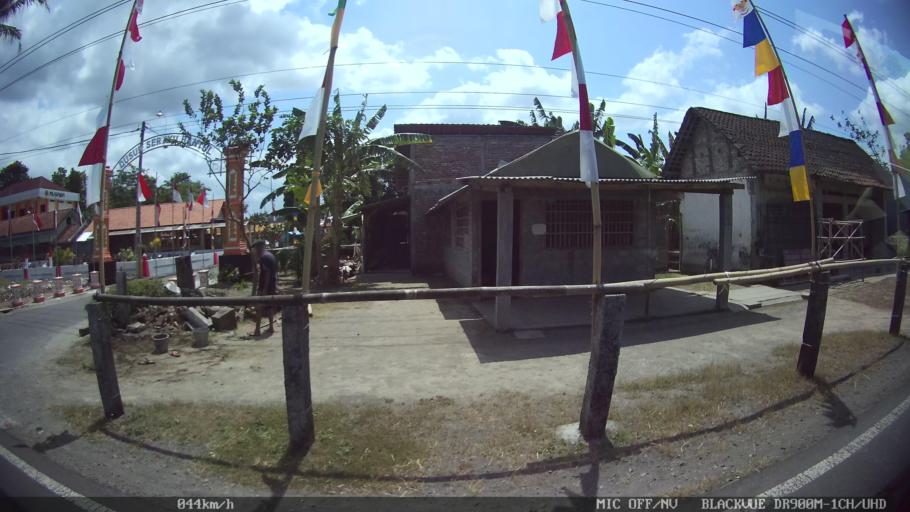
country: ID
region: Daerah Istimewa Yogyakarta
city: Bantul
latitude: -7.9047
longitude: 110.3345
